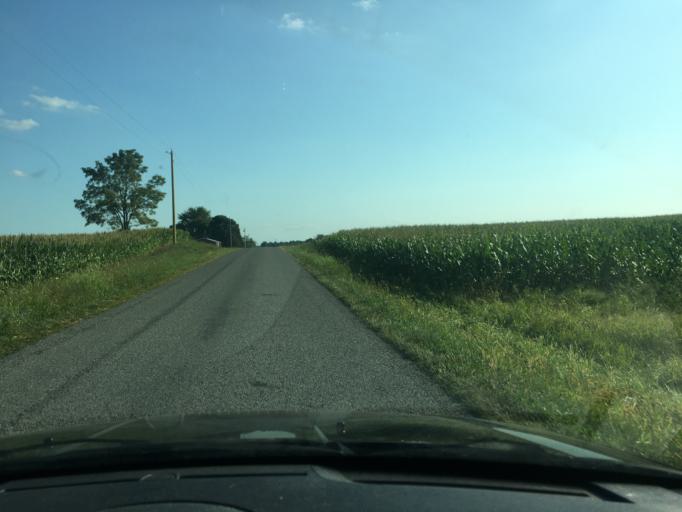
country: US
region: Ohio
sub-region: Logan County
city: West Liberty
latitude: 40.2545
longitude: -83.8037
